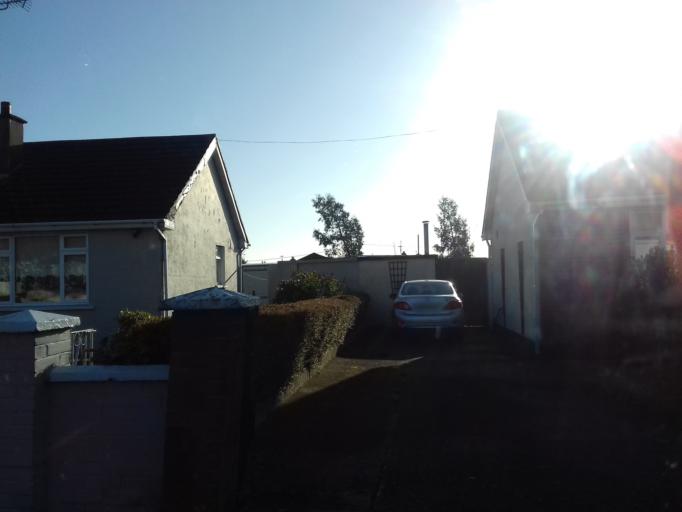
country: IE
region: Leinster
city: Beaumont
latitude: 53.4082
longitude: -6.2336
